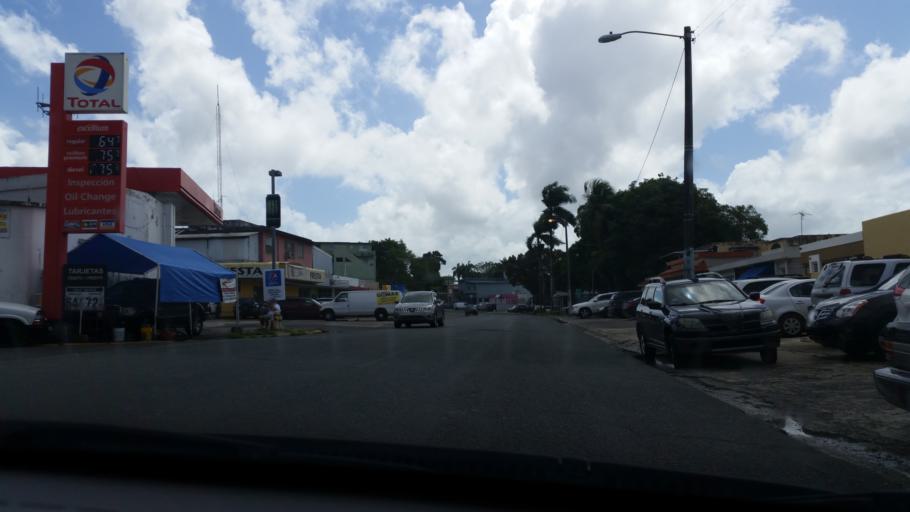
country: PR
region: Catano
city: Catano
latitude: 18.4064
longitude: -66.0940
